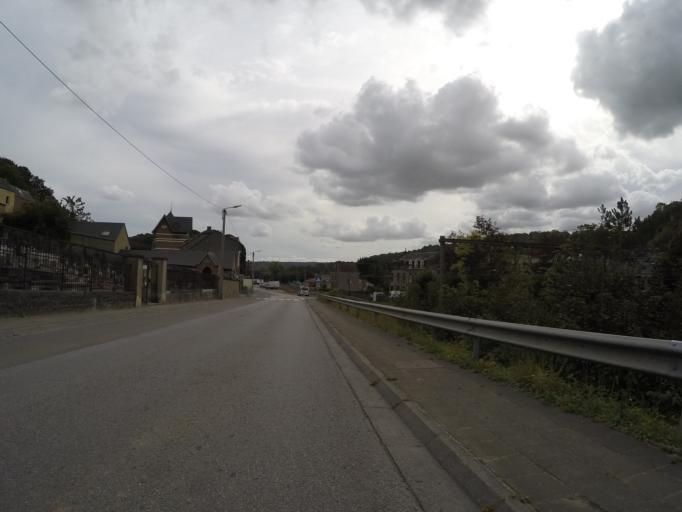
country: BE
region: Wallonia
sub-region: Province de Namur
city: Yvoir
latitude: 50.3299
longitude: 4.8753
